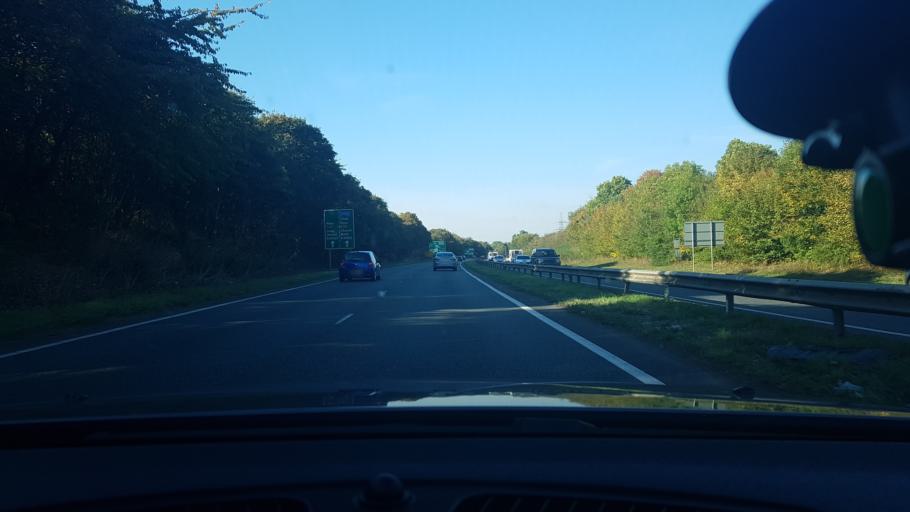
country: GB
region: England
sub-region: Gloucestershire
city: Barnwood
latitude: 51.8716
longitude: -2.1980
